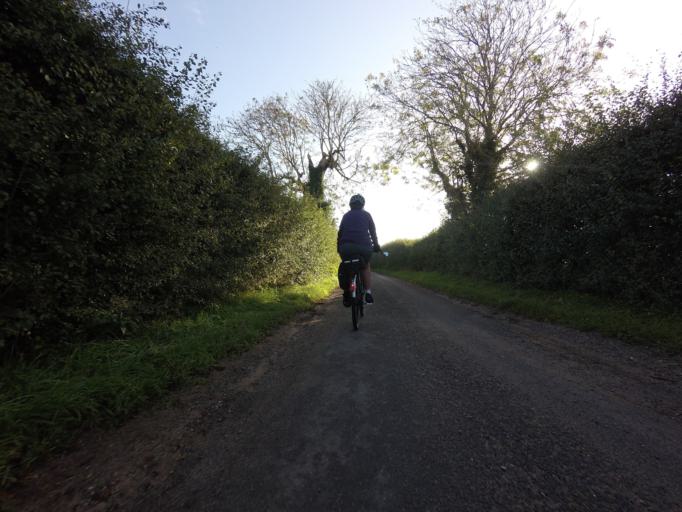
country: GB
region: England
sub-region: Norfolk
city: Dersingham
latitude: 52.8208
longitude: 0.5235
